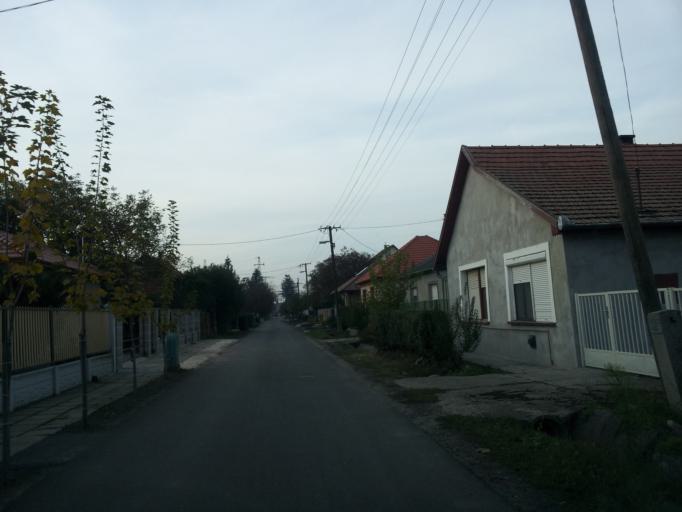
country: HU
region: Pest
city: Nagykata
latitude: 47.4230
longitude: 19.7436
